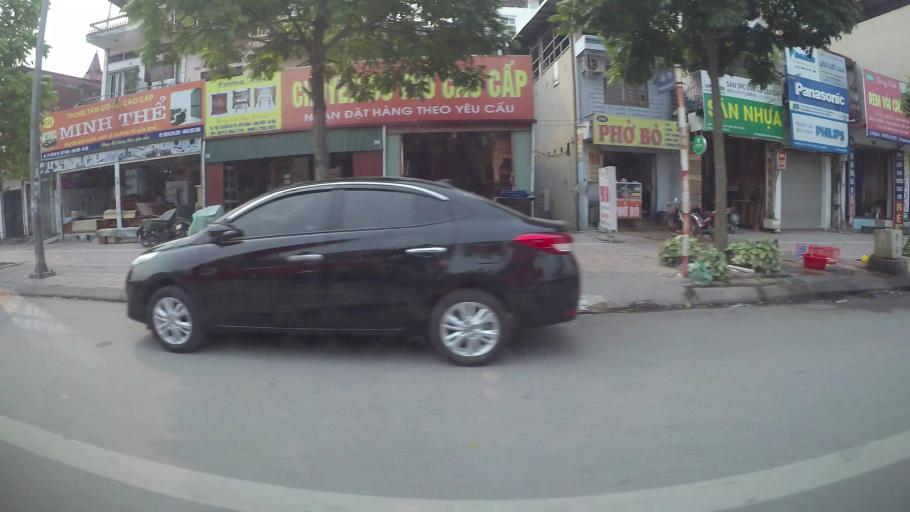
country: VN
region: Ha Noi
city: Trau Quy
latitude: 21.0690
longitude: 105.9010
